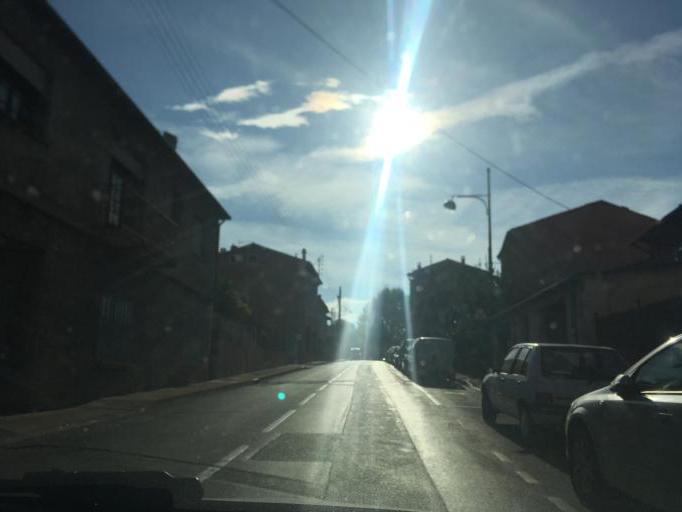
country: FR
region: Provence-Alpes-Cote d'Azur
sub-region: Departement du Var
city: Draguignan
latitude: 43.5415
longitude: 6.4665
